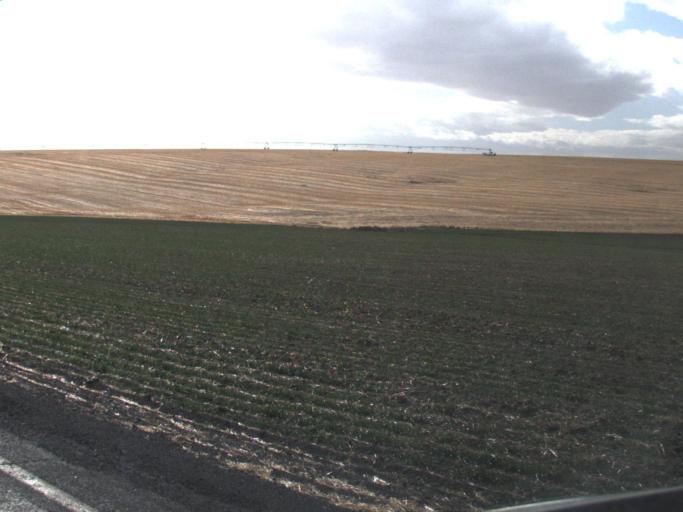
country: US
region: Washington
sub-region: Okanogan County
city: Coulee Dam
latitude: 47.4939
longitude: -118.7848
